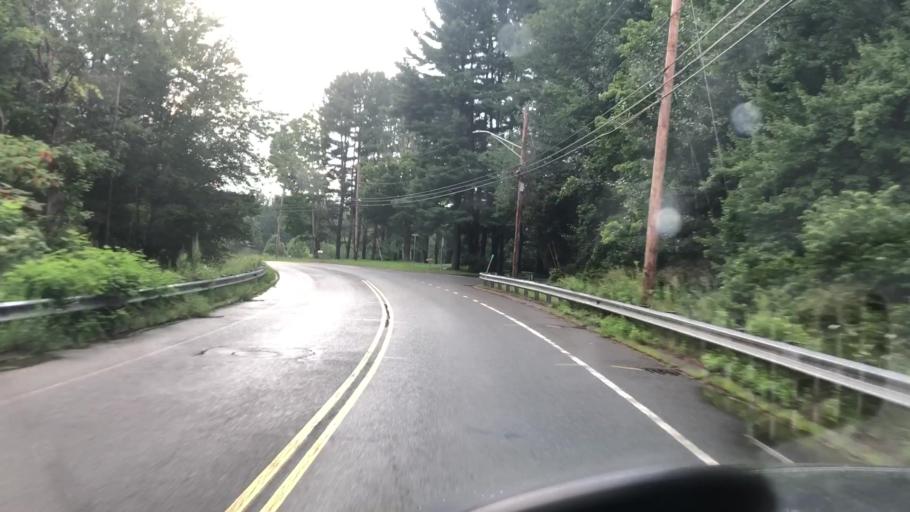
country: US
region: Massachusetts
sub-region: Hampshire County
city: Easthampton
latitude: 42.3029
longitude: -72.6844
